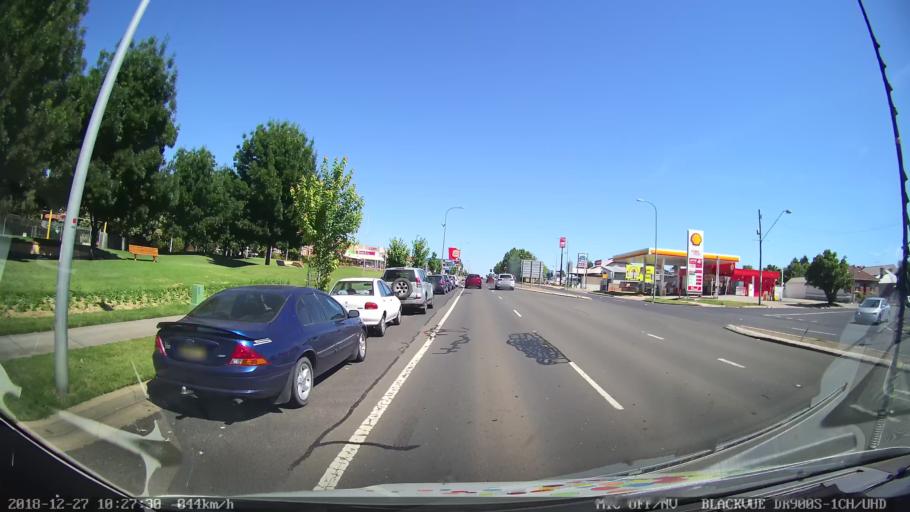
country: AU
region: New South Wales
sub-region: Bathurst Regional
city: Bathurst
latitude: -33.4171
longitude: 149.5844
